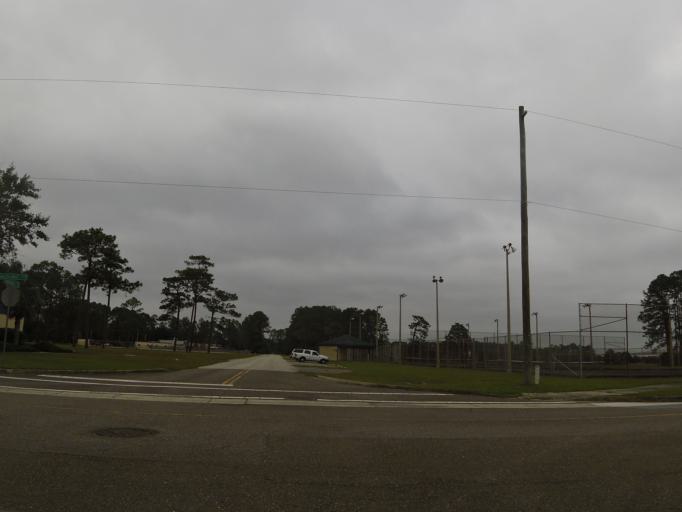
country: US
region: Florida
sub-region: Duval County
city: Baldwin
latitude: 30.2255
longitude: -81.8873
